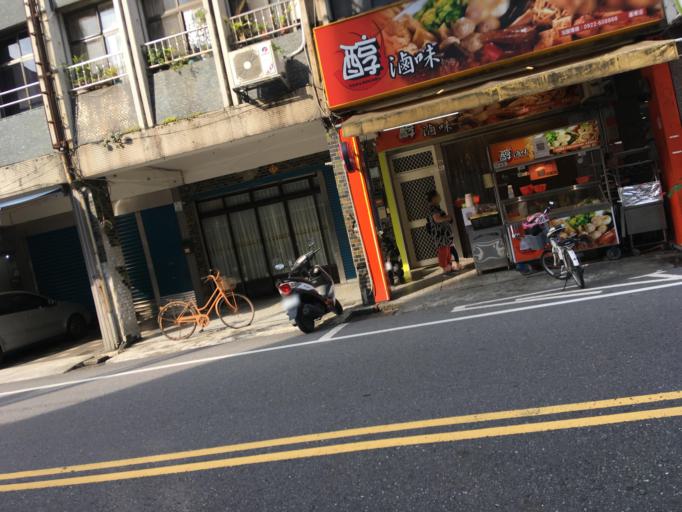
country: TW
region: Taiwan
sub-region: Yilan
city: Yilan
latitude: 24.6711
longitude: 121.7708
